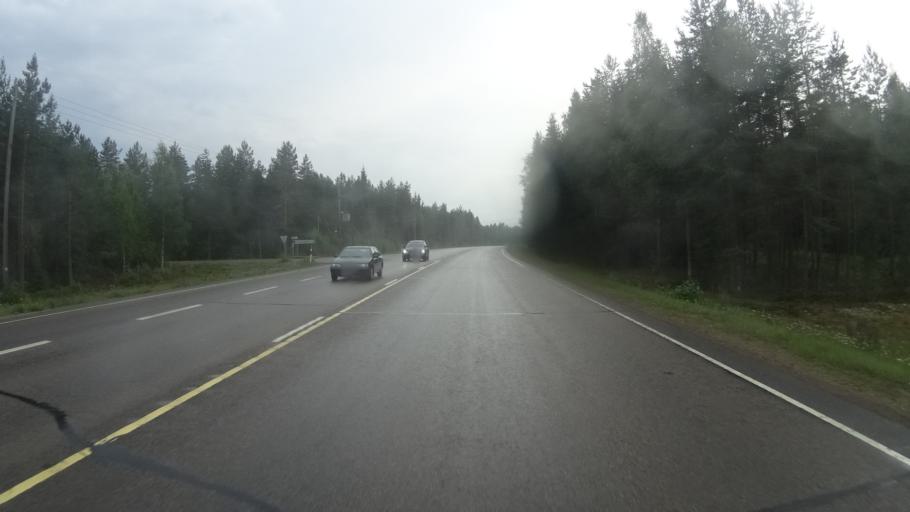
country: FI
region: Kymenlaakso
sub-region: Kouvola
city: Anjala
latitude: 60.7215
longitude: 26.8546
